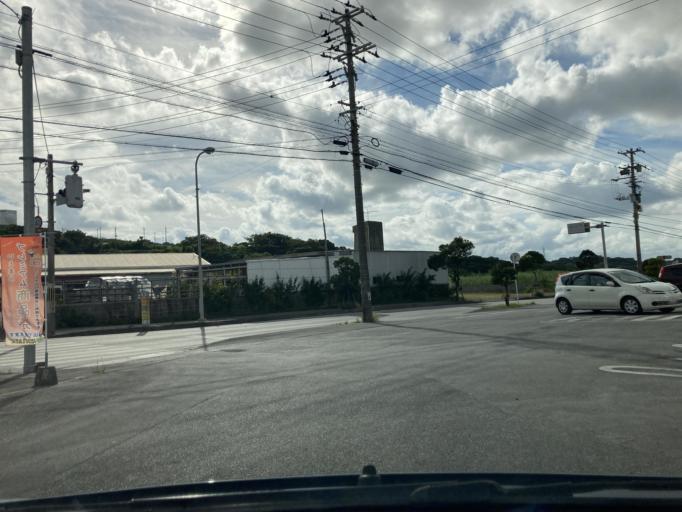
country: JP
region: Okinawa
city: Itoman
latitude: 26.1350
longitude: 127.7100
